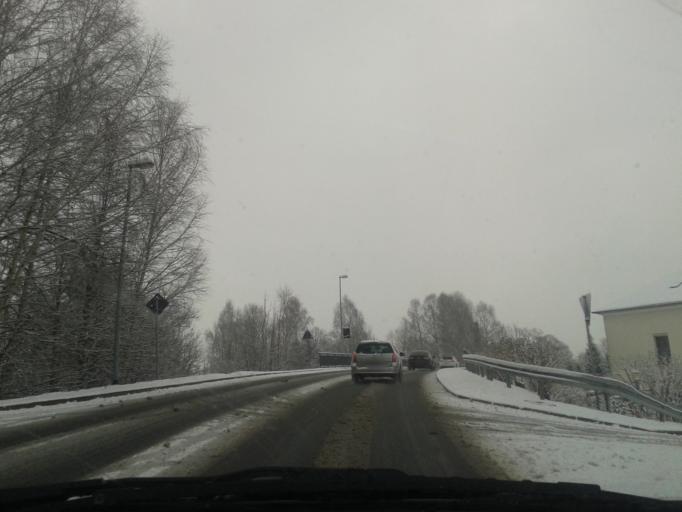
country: DE
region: Saxony
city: Grossharthau
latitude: 51.1024
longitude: 14.0920
